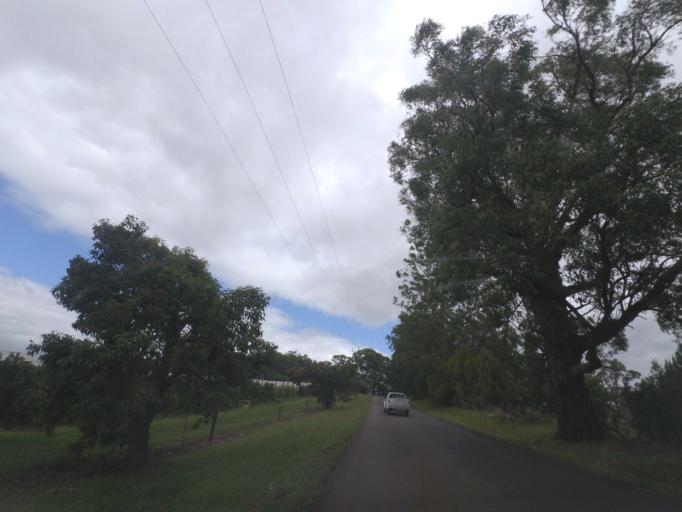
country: AU
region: Victoria
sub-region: Yarra Ranges
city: Yarra Junction
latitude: -37.8402
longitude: 145.5910
